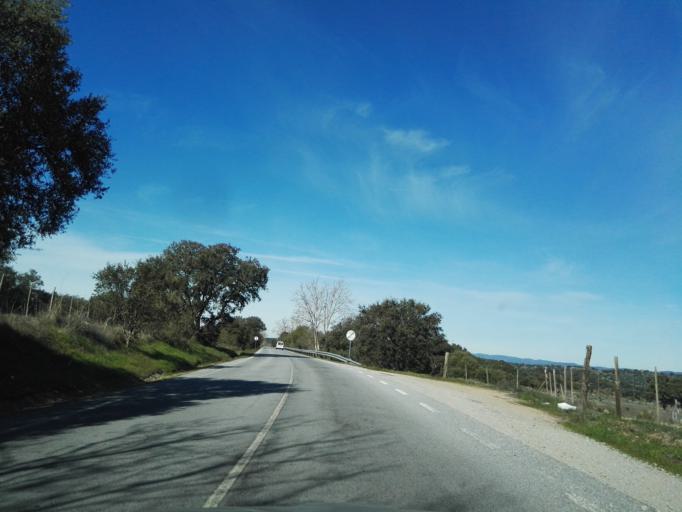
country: PT
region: Portalegre
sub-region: Arronches
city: Arronches
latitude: 39.0438
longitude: -7.2614
